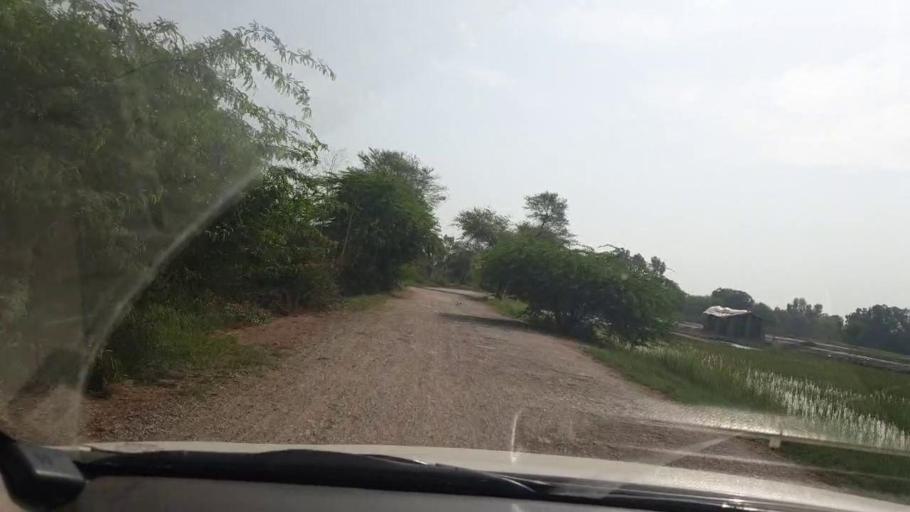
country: PK
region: Sindh
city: Lakhi
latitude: 27.8309
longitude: 68.7566
